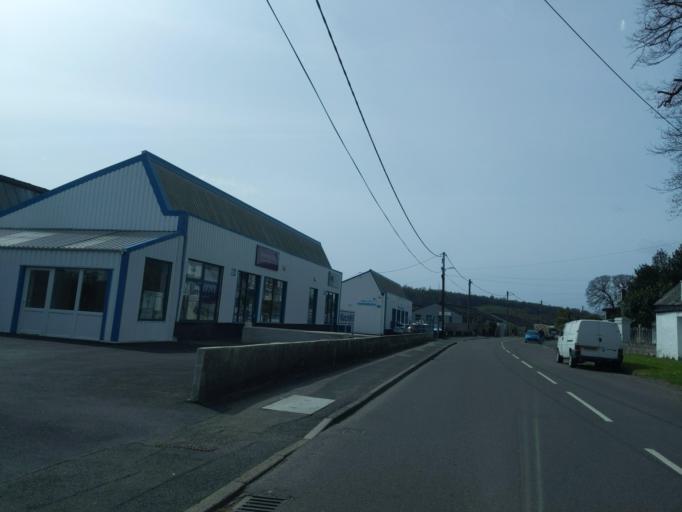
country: GB
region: England
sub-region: Devon
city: Plympton
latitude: 50.3950
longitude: -4.0508
